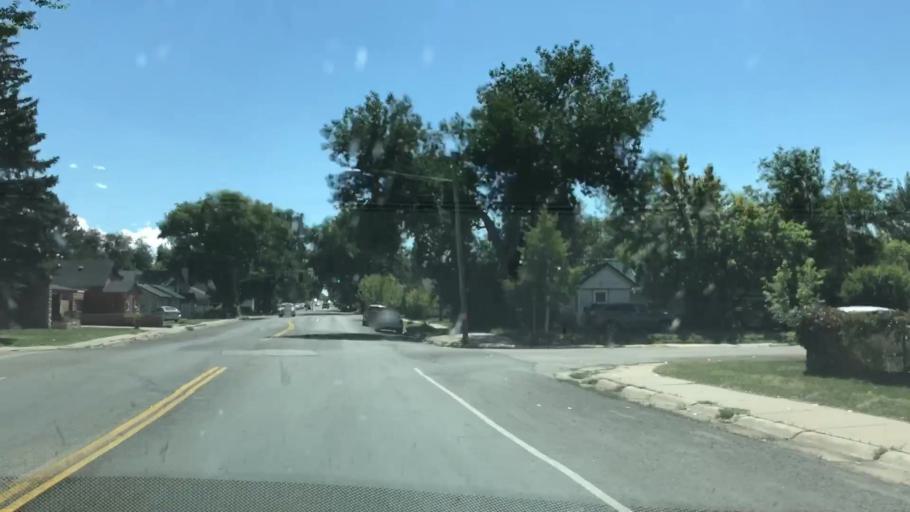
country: US
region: Wyoming
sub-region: Albany County
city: Laramie
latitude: 41.3202
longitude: -105.5847
